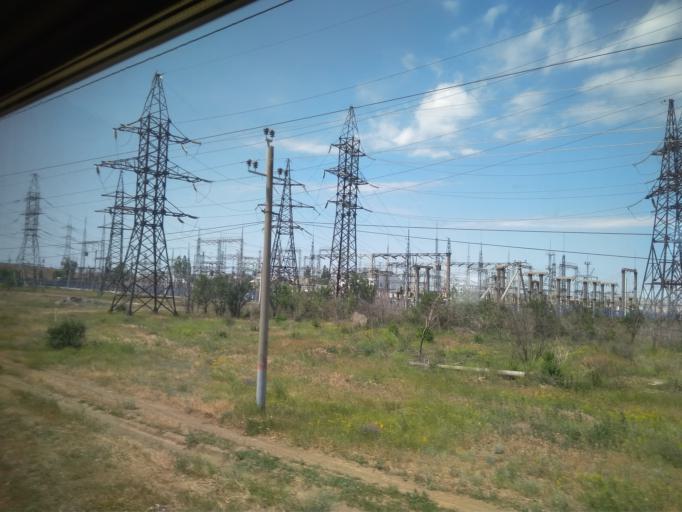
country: RU
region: Volgograd
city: Gumrak
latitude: 48.7604
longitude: 44.4243
